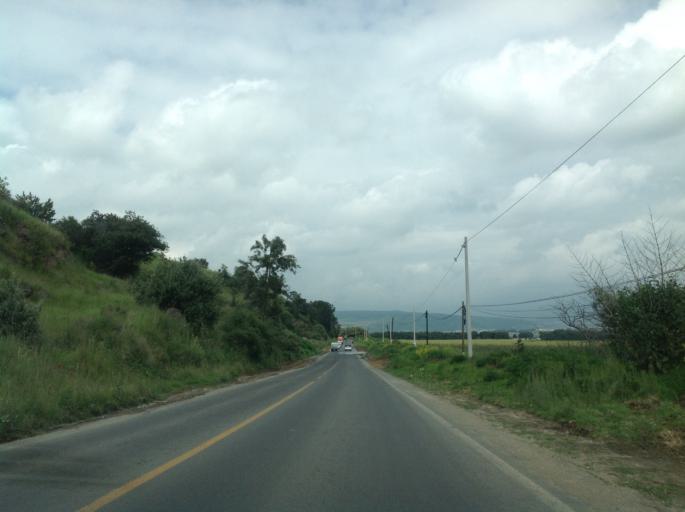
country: MX
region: Mexico
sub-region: Tenango del Valle
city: Santa Maria Jajalpa
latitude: 19.1175
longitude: -99.5553
